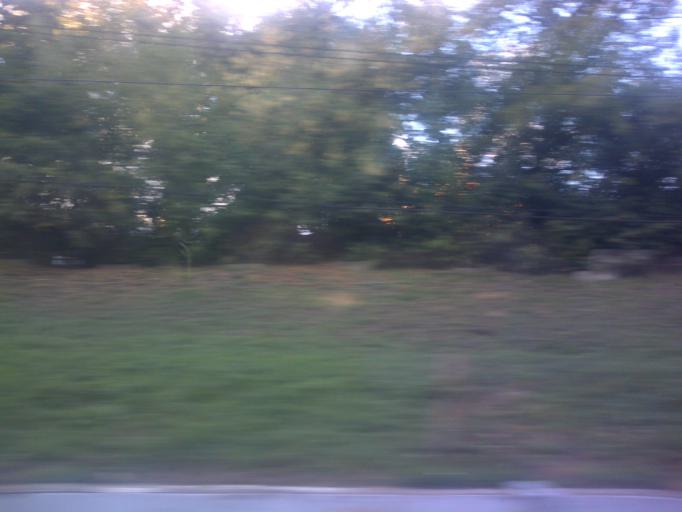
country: RU
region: Moscow
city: Taganskiy
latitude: 55.7641
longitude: 37.6587
